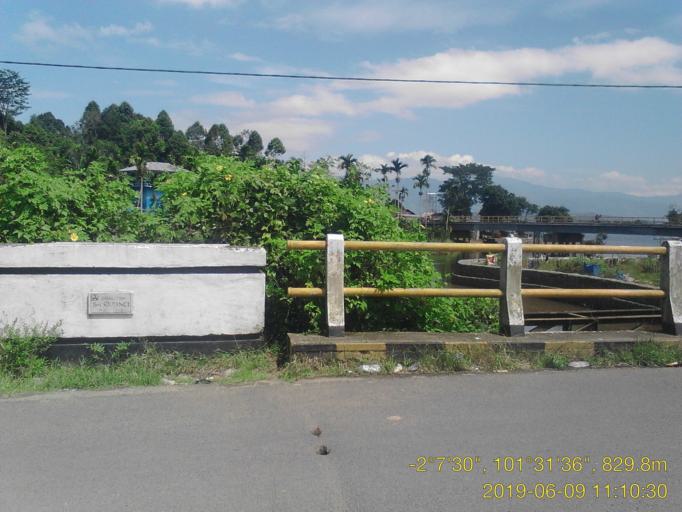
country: ID
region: Jambi
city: Sungai Penuh
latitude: -2.1250
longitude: 101.5270
